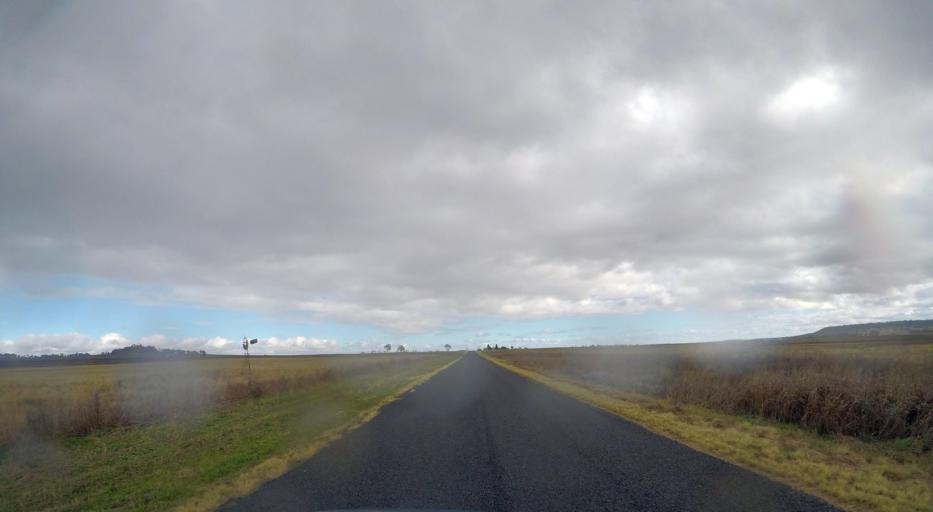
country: AU
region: Queensland
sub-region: Southern Downs
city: Warwick
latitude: -28.0487
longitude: 152.0404
